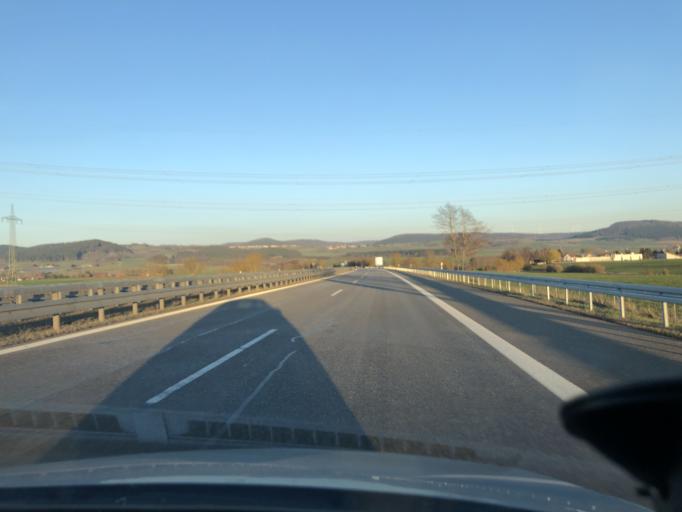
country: DE
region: Baden-Wuerttemberg
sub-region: Freiburg Region
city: Tuningen
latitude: 47.9942
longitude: 8.5729
